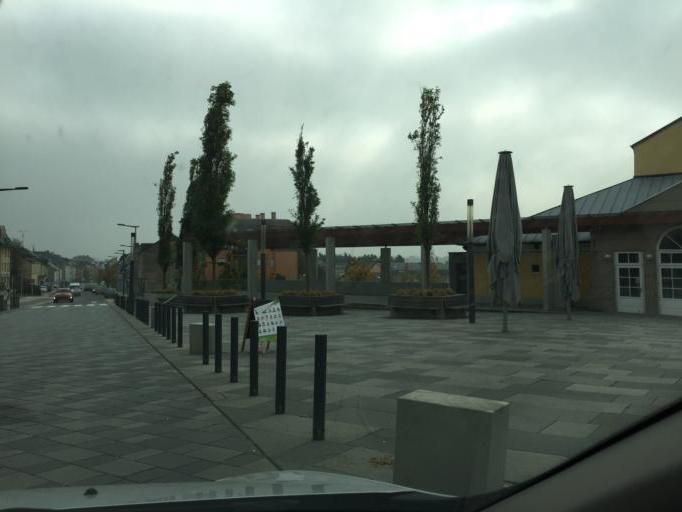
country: LU
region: Luxembourg
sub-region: Canton de Luxembourg
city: Sandweiler
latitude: 49.6164
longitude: 6.2189
